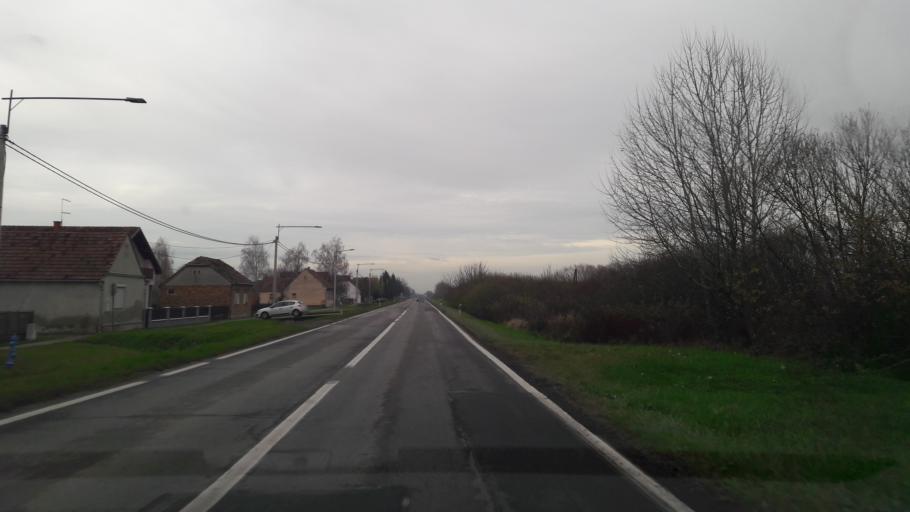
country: HR
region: Osjecko-Baranjska
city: Bizovac
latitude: 45.5788
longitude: 18.4230
